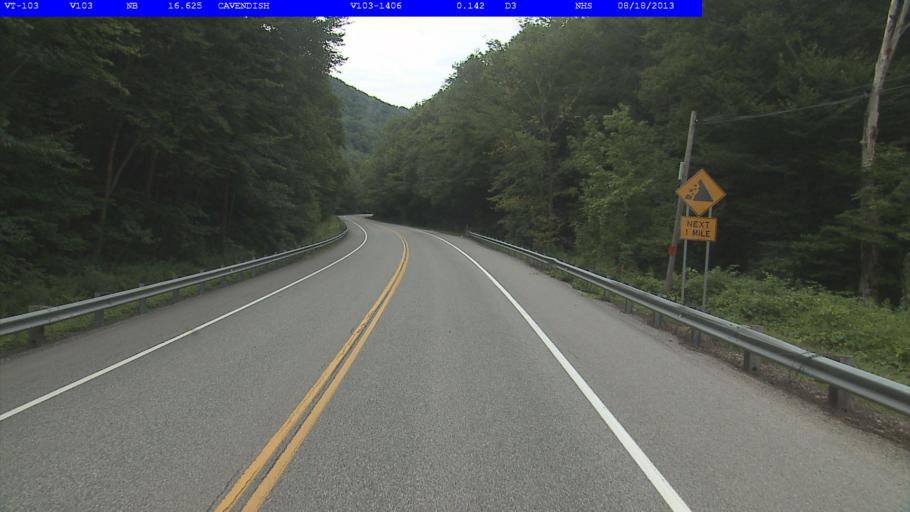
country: US
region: Vermont
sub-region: Windsor County
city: Chester
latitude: 43.3511
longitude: -72.6271
